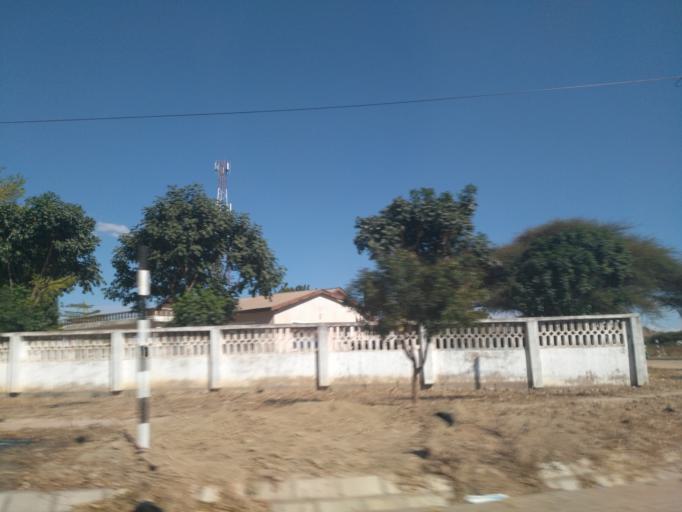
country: TZ
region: Dodoma
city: Dodoma
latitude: -6.1956
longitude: 35.7348
